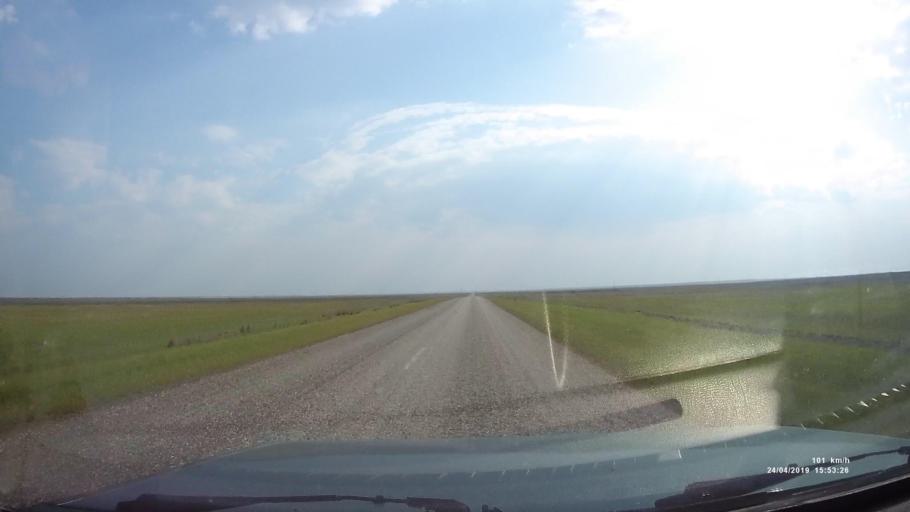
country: RU
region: Kalmykiya
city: Yashalta
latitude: 46.5981
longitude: 42.5756
